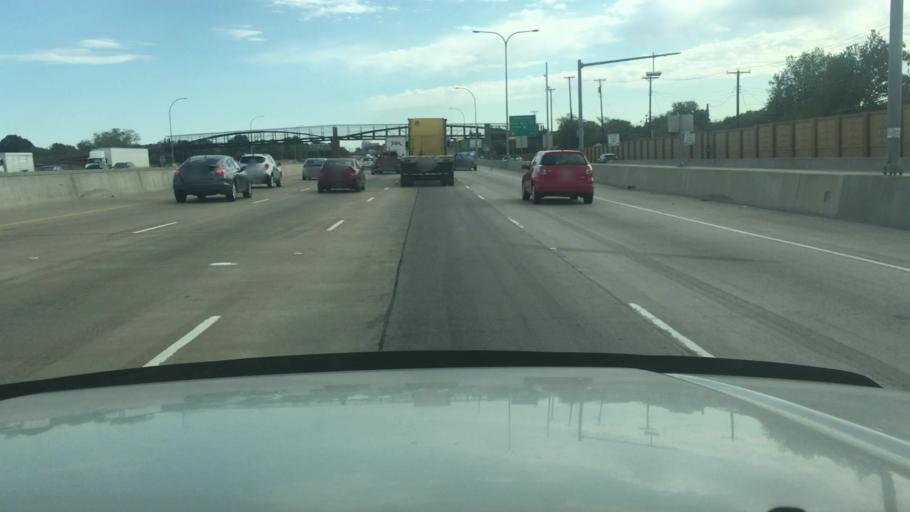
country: US
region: Texas
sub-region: Dallas County
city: Farmers Branch
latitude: 32.9144
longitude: -96.8669
